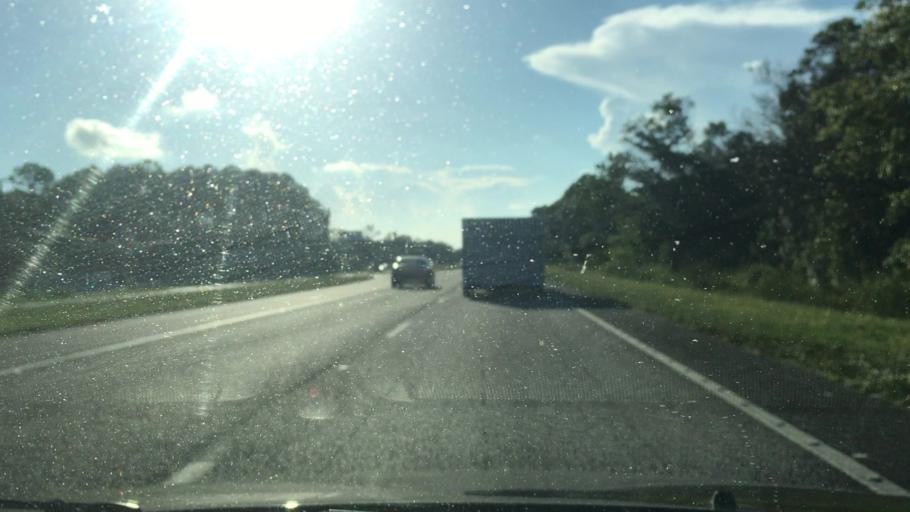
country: US
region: Florida
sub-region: Orange County
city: Christmas
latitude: 28.5370
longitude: -80.9973
